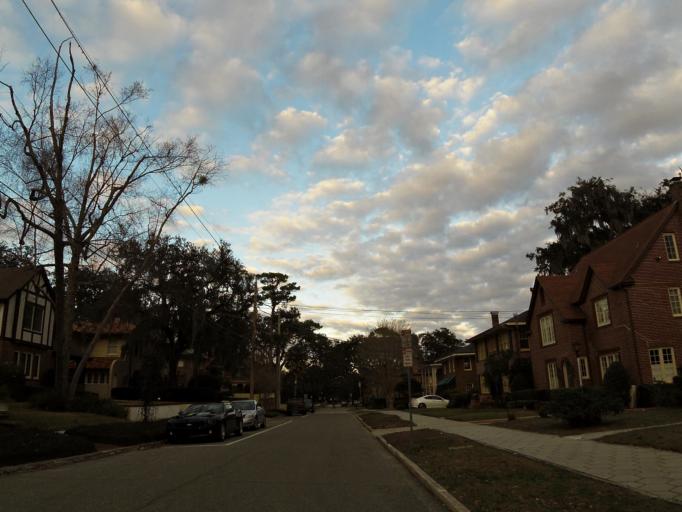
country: US
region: Florida
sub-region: Duval County
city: Jacksonville
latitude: 30.2969
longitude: -81.7022
